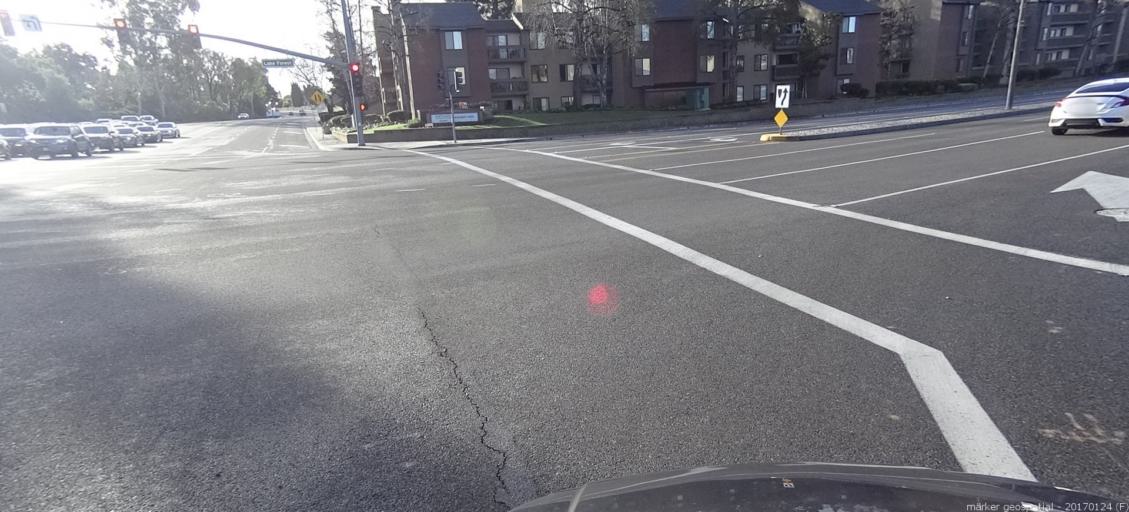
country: US
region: California
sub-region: Orange County
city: Laguna Hills
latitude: 33.6343
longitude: -117.7100
